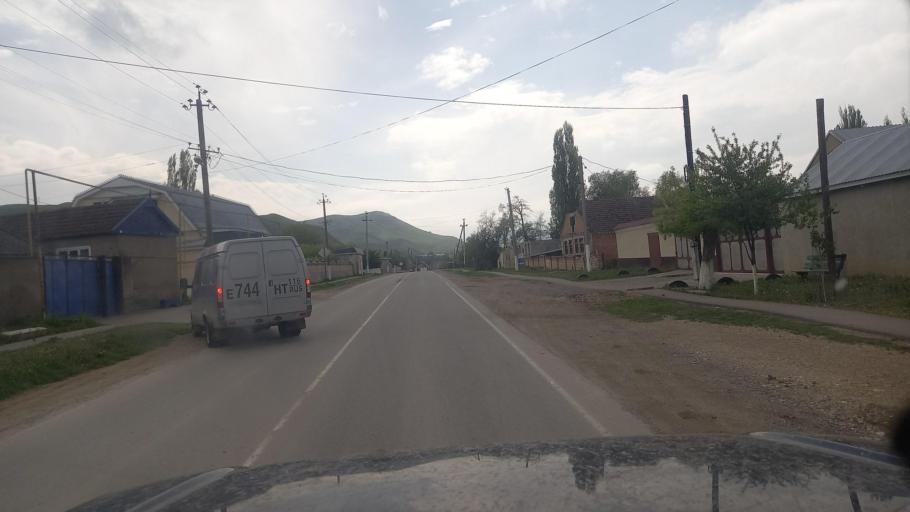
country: RU
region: Kabardino-Balkariya
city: Sarmakovo
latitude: 43.7320
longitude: 43.1707
